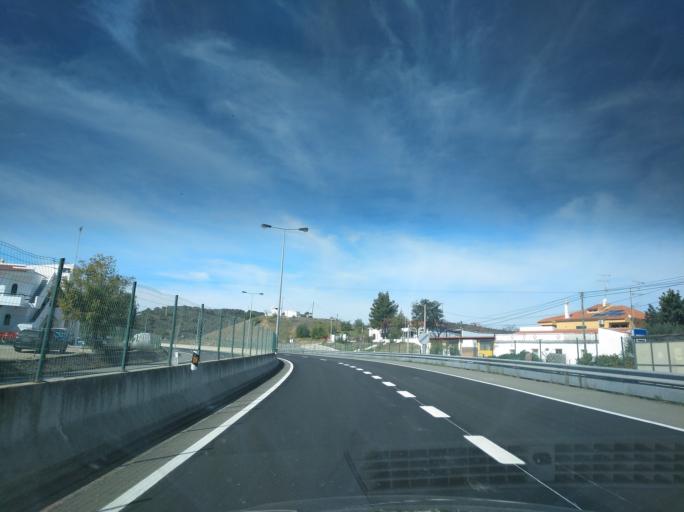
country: PT
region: Faro
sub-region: Castro Marim
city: Castro Marim
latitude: 37.3338
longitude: -7.4902
